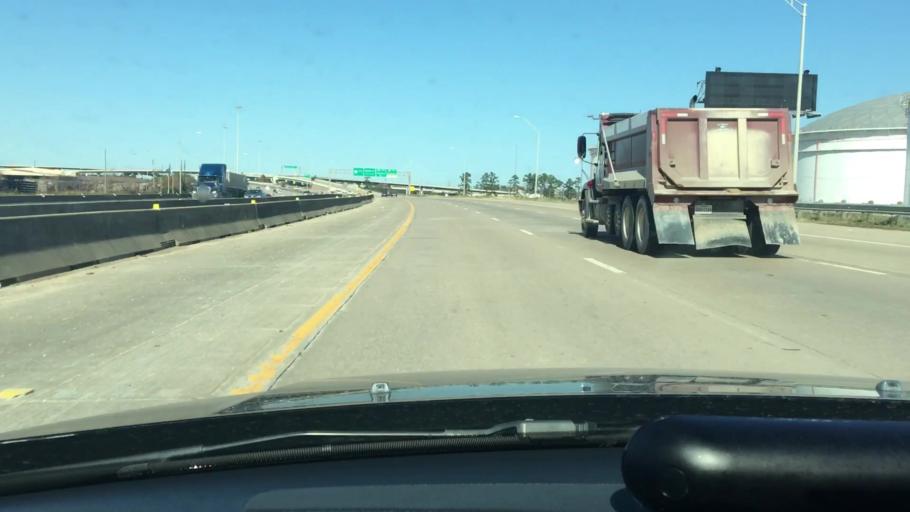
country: US
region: Texas
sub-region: Harris County
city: Cloverleaf
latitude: 29.7622
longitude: -95.1468
